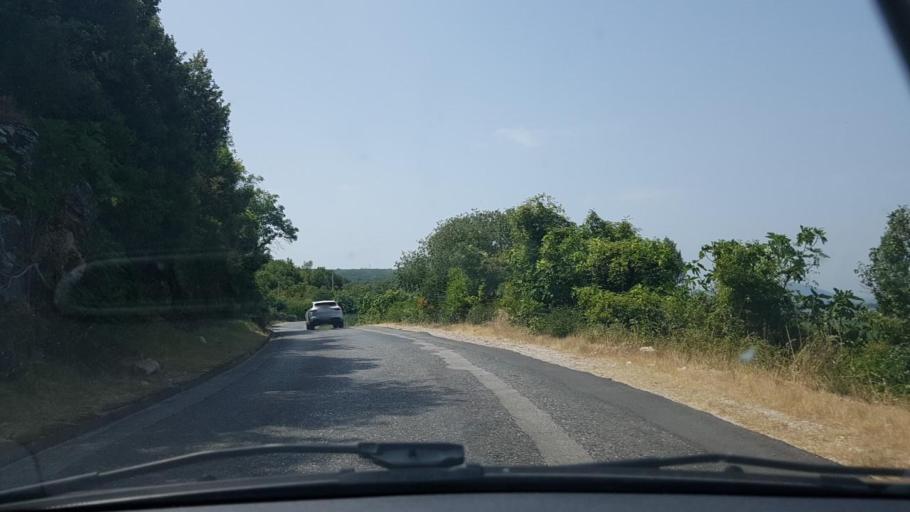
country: BA
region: Federation of Bosnia and Herzegovina
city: Tasovcici
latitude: 43.0202
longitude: 17.7673
